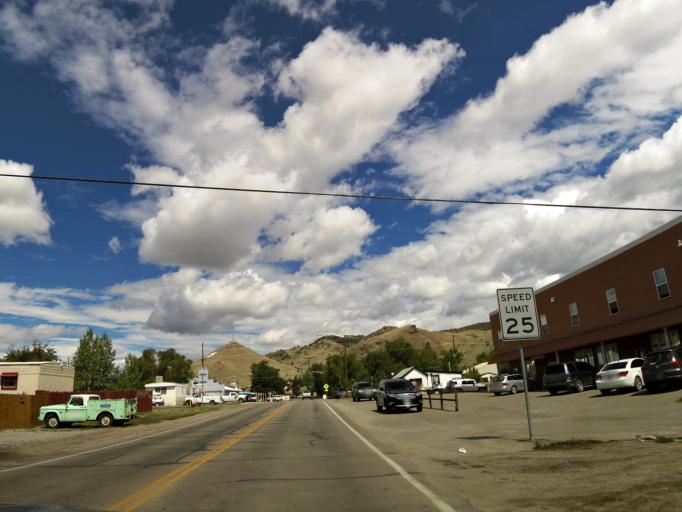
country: US
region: Colorado
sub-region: Chaffee County
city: Salida
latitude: 38.5295
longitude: -105.9847
